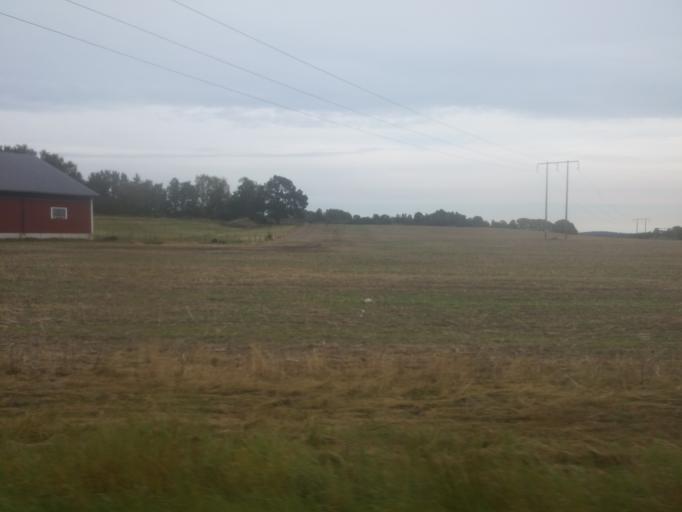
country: SE
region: OEstergoetland
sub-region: Norrkopings Kommun
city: Krokek
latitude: 58.5777
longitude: 16.3962
